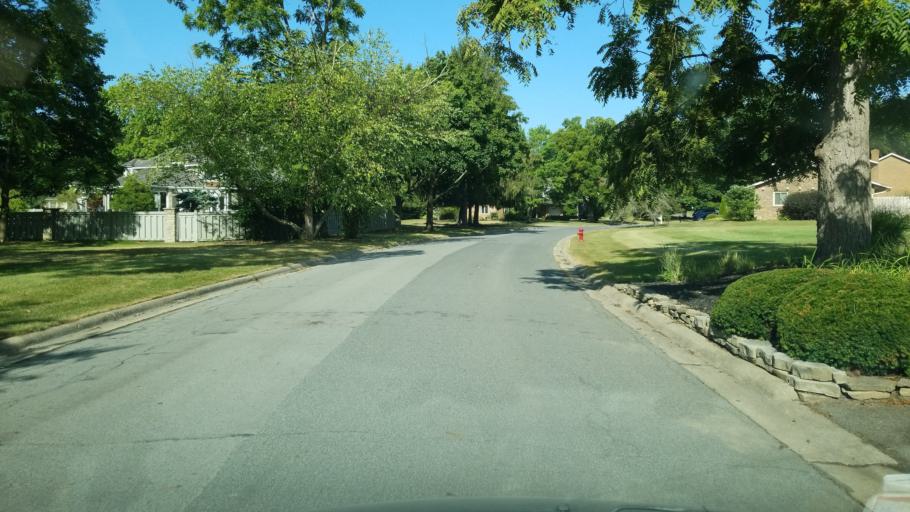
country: US
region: Ohio
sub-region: Delaware County
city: Powell
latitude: 40.1280
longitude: -83.0445
